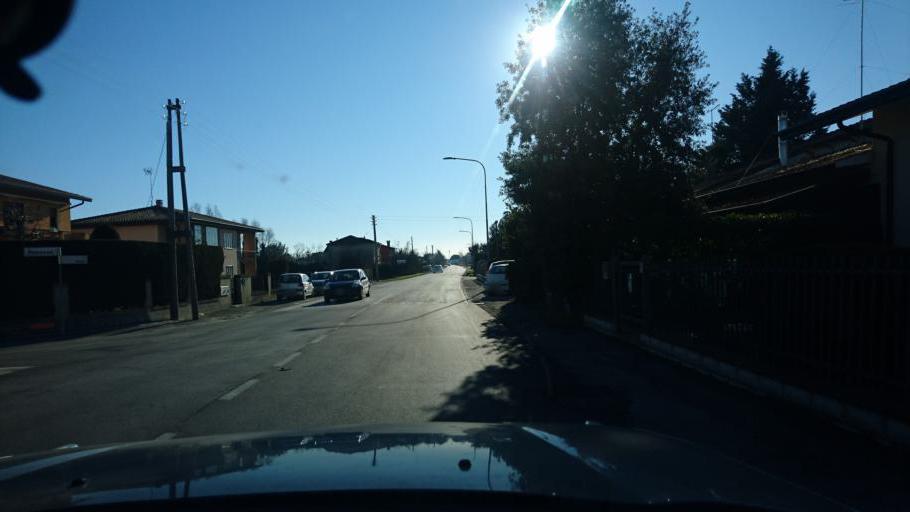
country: IT
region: Veneto
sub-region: Provincia di Rovigo
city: Porto Viro
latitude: 45.0361
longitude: 12.2270
